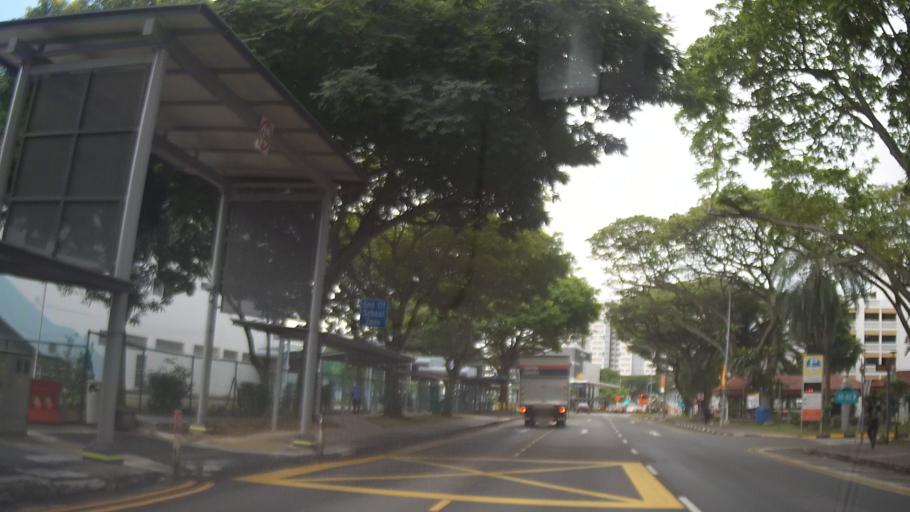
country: SG
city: Singapore
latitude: 1.3275
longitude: 103.8877
